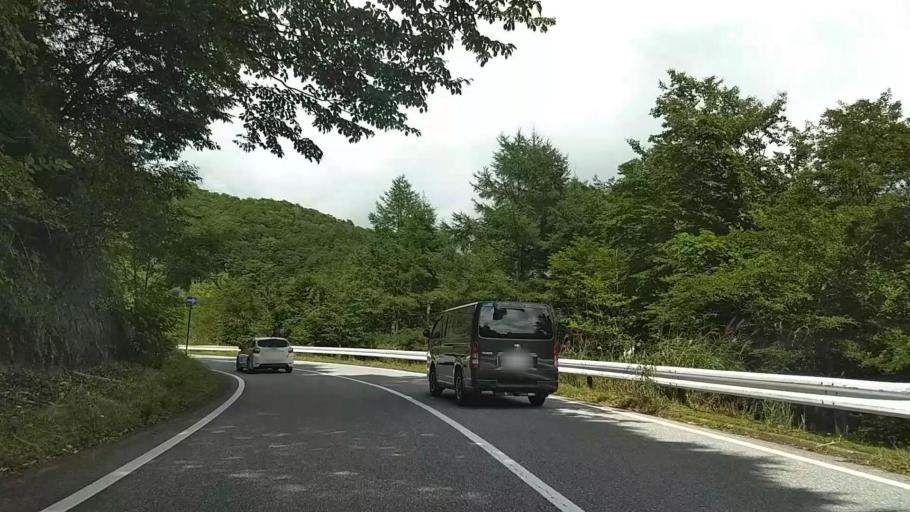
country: JP
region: Tochigi
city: Nikko
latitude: 36.7281
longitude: 139.5196
